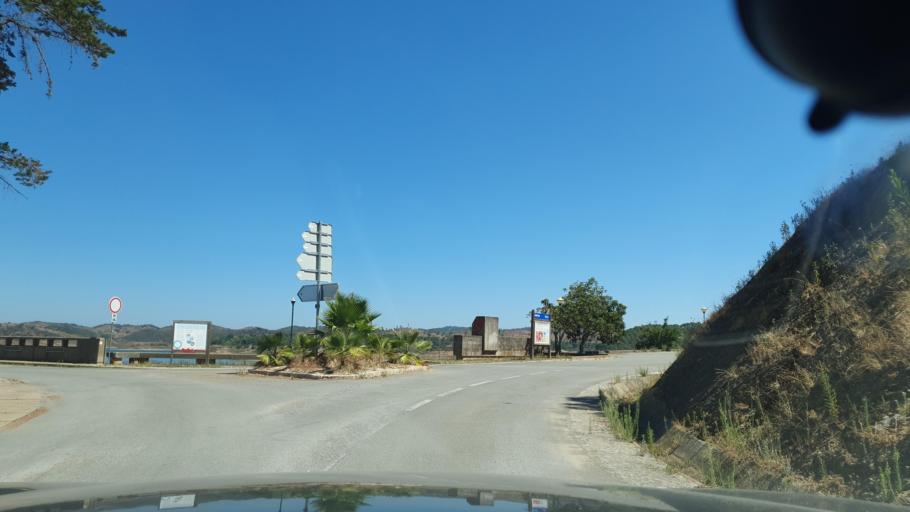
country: PT
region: Beja
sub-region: Odemira
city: Odemira
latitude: 37.5124
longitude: -8.4406
